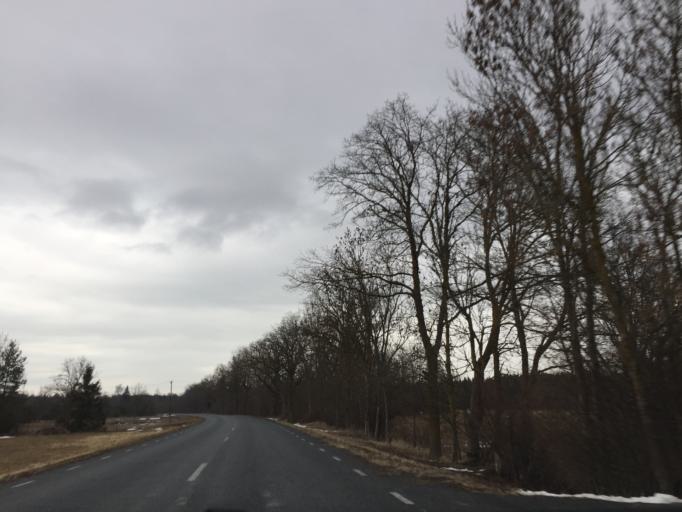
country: EE
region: Saare
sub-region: Orissaare vald
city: Orissaare
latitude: 58.5562
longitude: 22.7747
